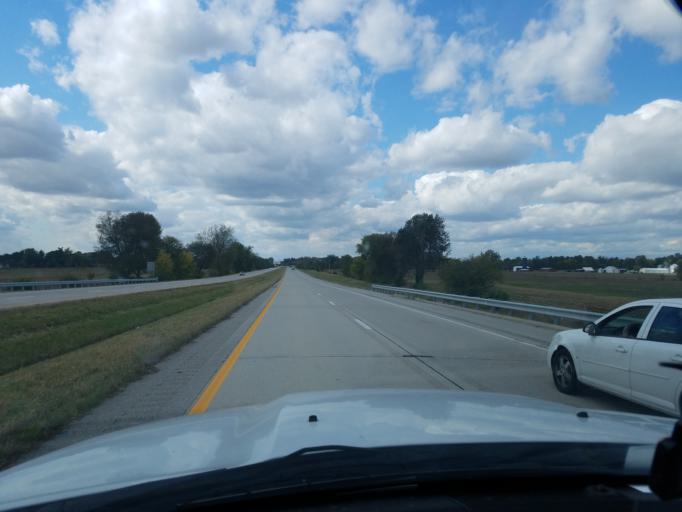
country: US
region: Kentucky
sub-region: Daviess County
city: Owensboro
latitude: 37.7665
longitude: -87.1790
